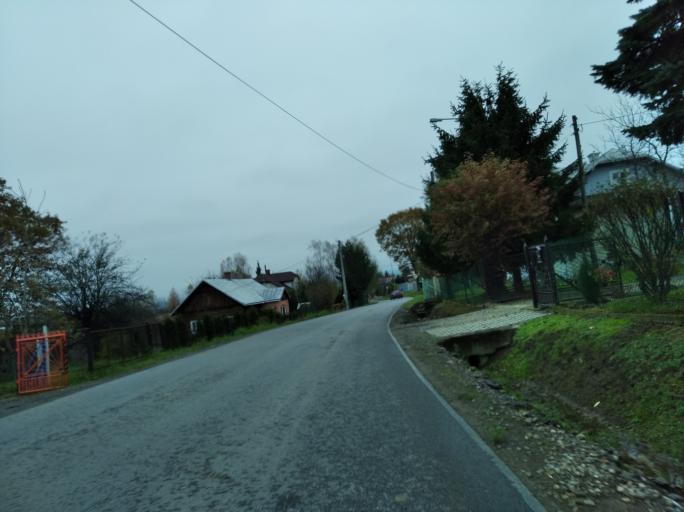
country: PL
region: Subcarpathian Voivodeship
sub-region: Powiat krosnienski
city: Jedlicze
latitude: 49.7311
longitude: 21.6504
